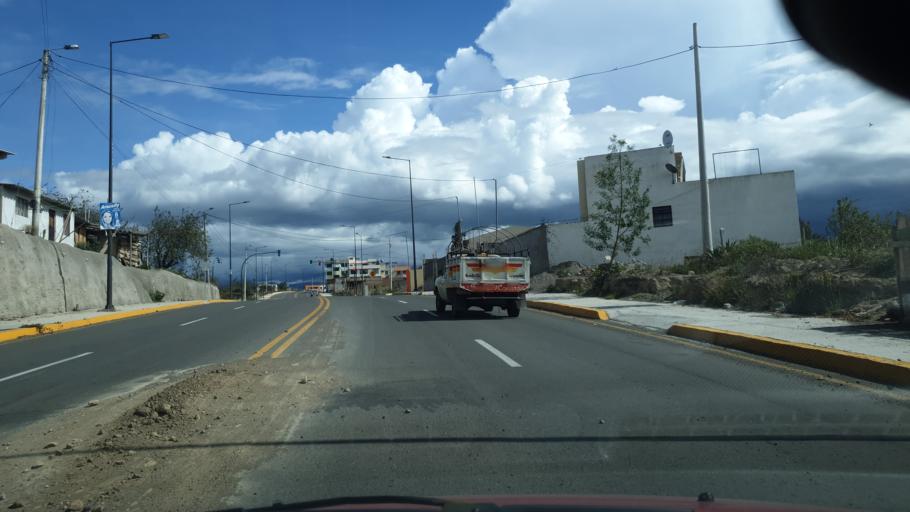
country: EC
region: Tungurahua
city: Ambato
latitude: -1.2942
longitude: -78.6310
